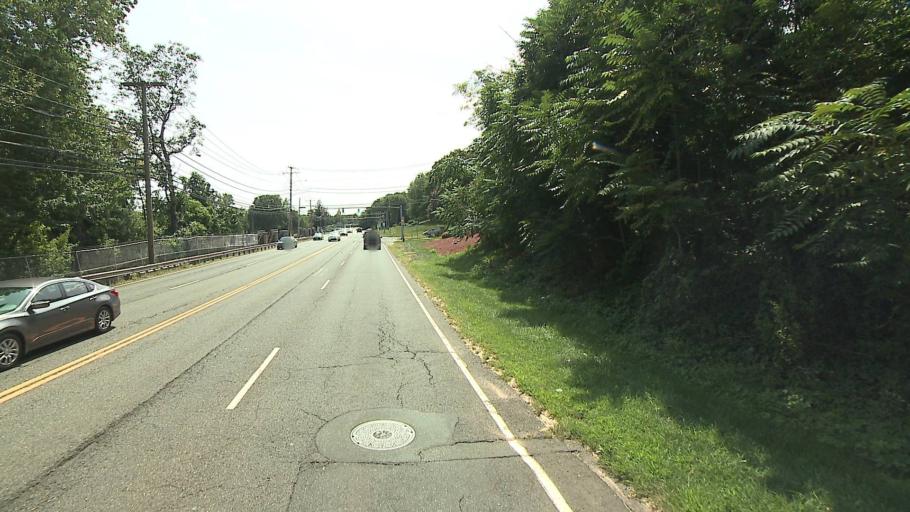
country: US
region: Connecticut
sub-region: New Haven County
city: City of Milford (balance)
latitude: 41.2489
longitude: -73.1013
